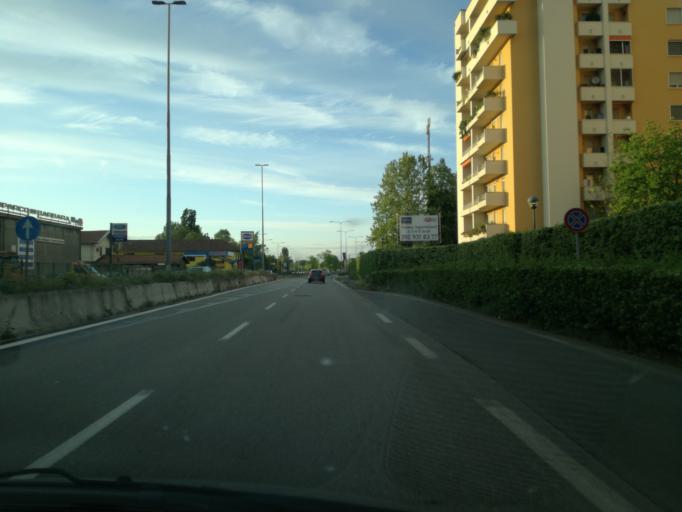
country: IT
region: Lombardy
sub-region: Citta metropolitana di Milano
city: Noverasco-Sporting Mirasole
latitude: 45.3959
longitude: 9.2108
